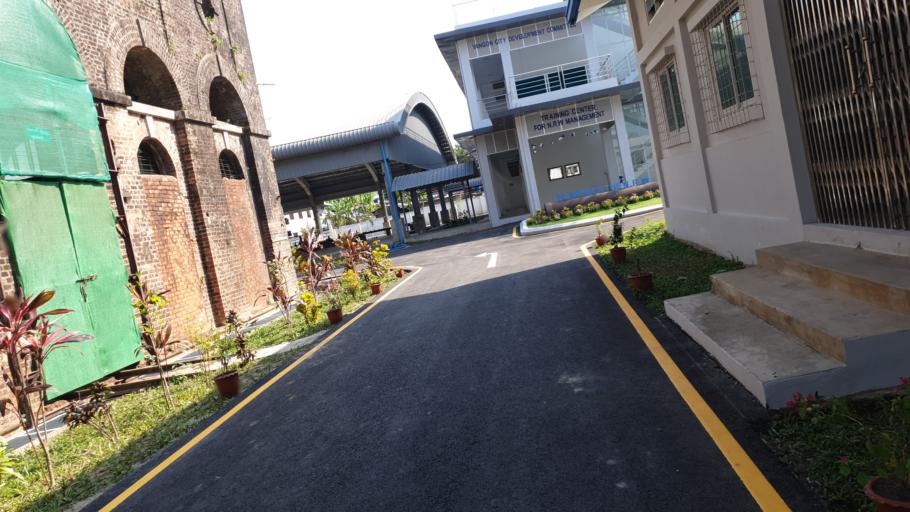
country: MM
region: Yangon
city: Yangon
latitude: 16.8585
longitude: 96.1588
